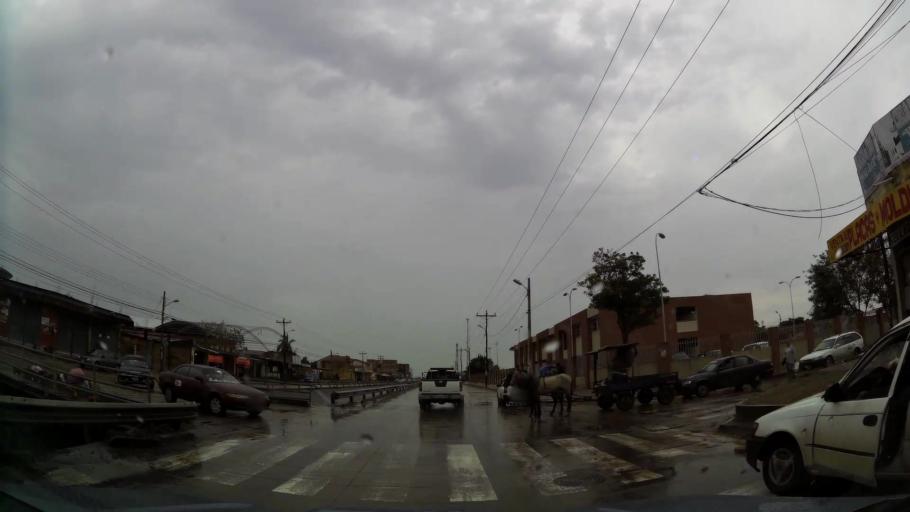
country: BO
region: Santa Cruz
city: Santa Cruz de la Sierra
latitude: -17.8020
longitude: -63.1310
